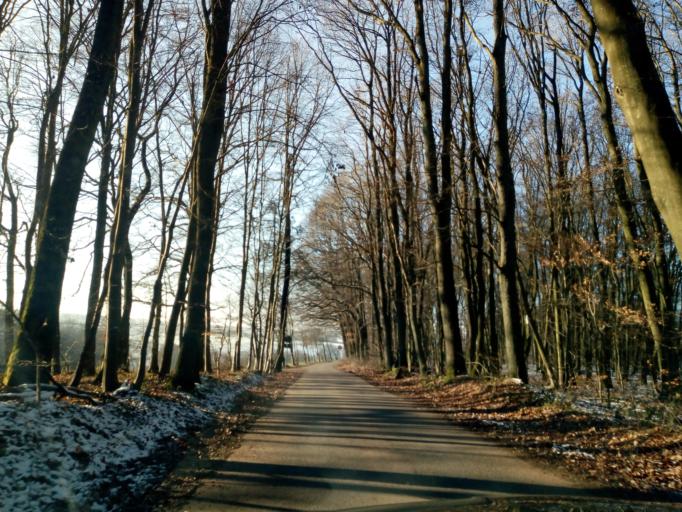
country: DE
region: Saarland
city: Heusweiler
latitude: 49.3633
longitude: 6.9546
